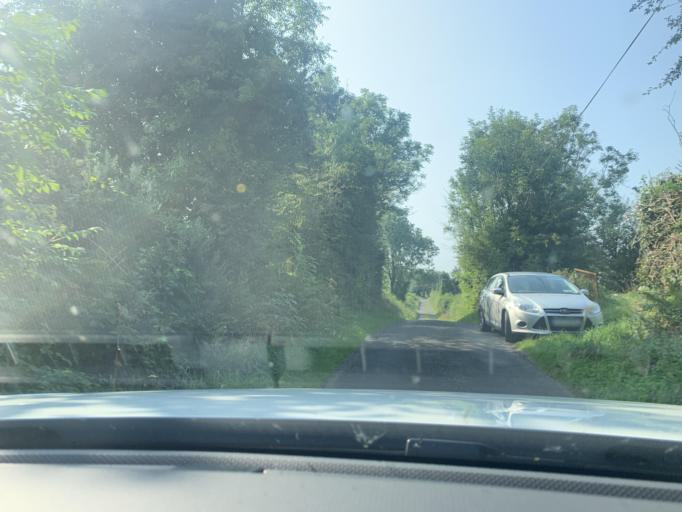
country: IE
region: Connaught
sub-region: Maigh Eo
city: Ballyhaunis
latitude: 53.8028
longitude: -8.7444
